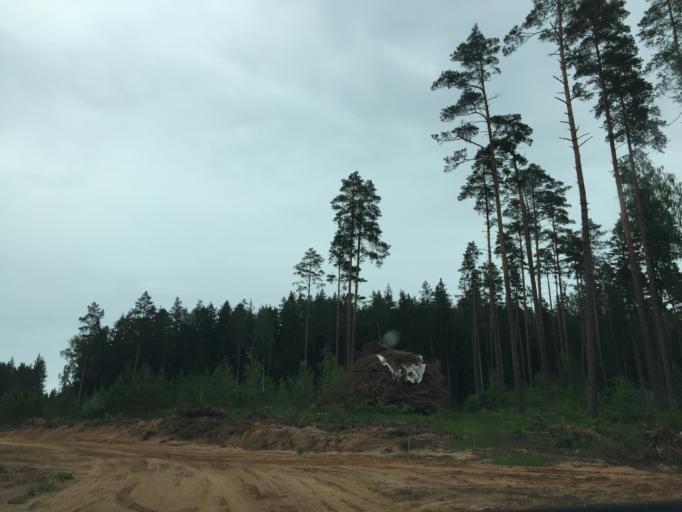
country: LV
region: Tukuma Rajons
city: Tukums
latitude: 57.0098
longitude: 23.1175
